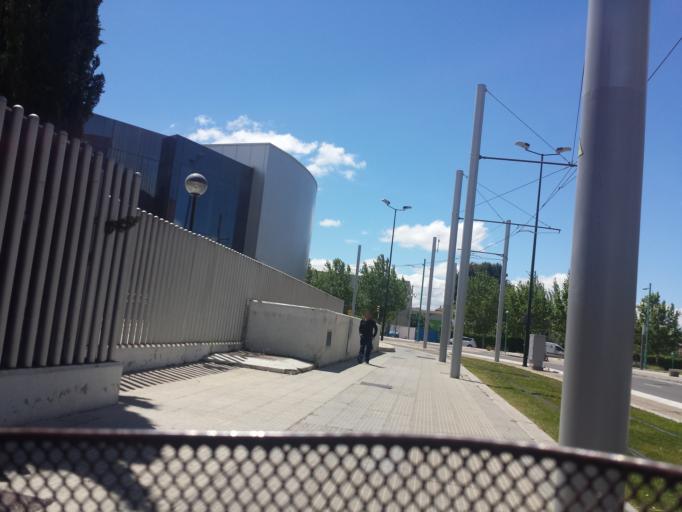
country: ES
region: Aragon
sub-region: Provincia de Zaragoza
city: Zaragoza
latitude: 41.6619
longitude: -0.8840
